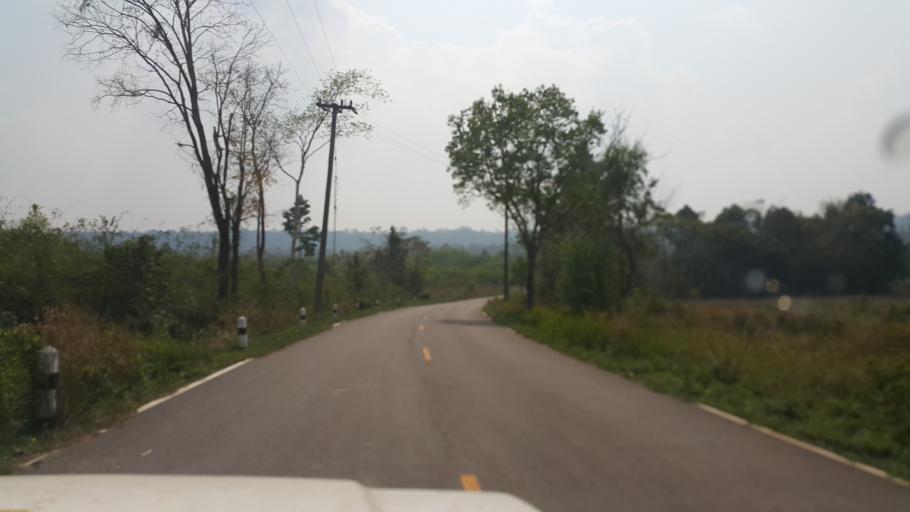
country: TH
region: Nakhon Phanom
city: Ban Phaeng
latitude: 17.9523
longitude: 104.1714
